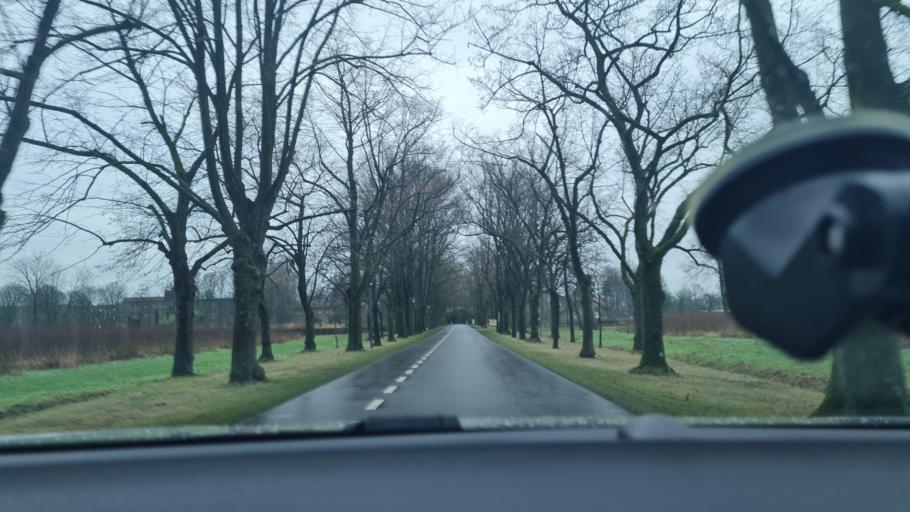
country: DE
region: North Rhine-Westphalia
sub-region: Regierungsbezirk Dusseldorf
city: Hunxe
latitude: 51.7016
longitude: 6.7459
